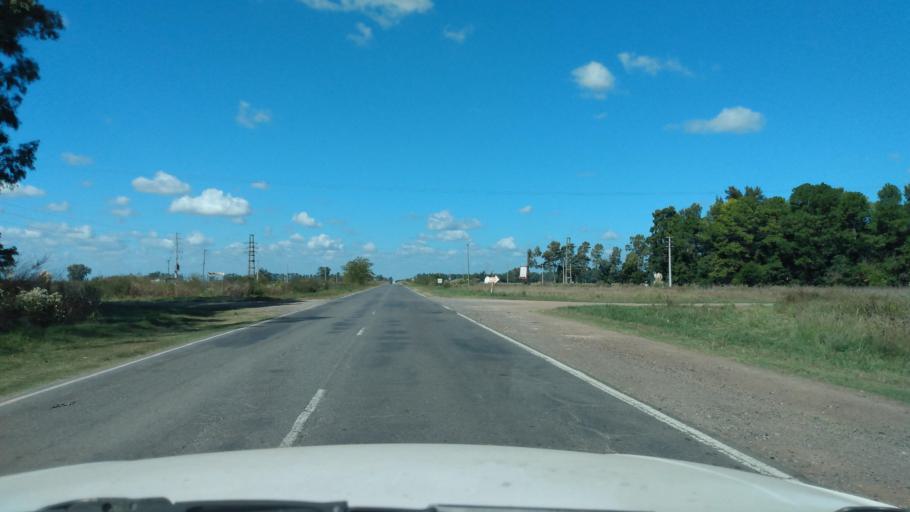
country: AR
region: Buenos Aires
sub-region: Partido de Mercedes
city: Mercedes
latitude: -34.7193
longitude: -59.3952
